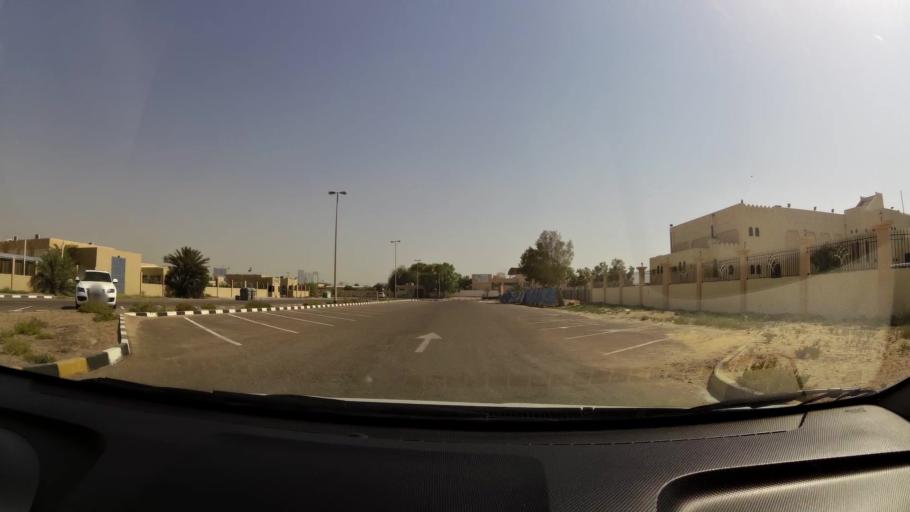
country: AE
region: Ajman
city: Ajman
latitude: 25.4143
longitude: 55.4710
